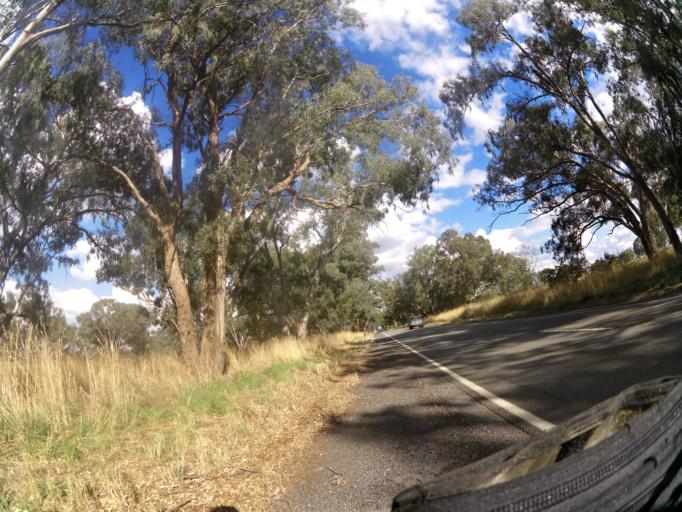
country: AU
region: Victoria
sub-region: Mansfield
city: Mansfield
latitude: -37.0104
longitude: 146.0843
